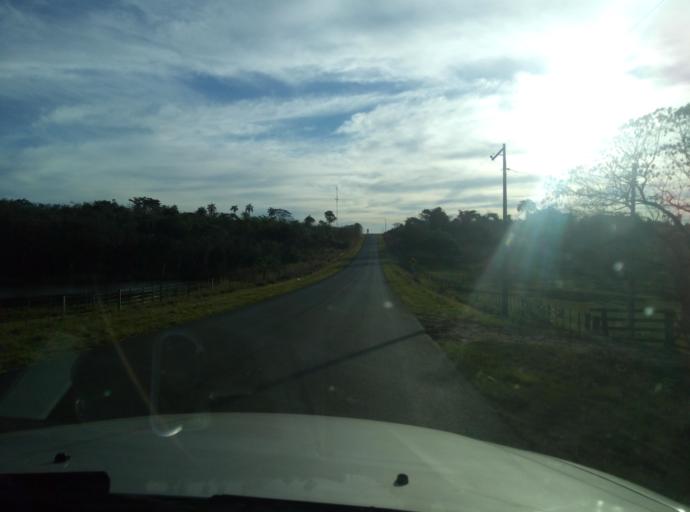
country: PY
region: Caaguazu
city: Carayao
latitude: -25.1540
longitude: -56.3194
